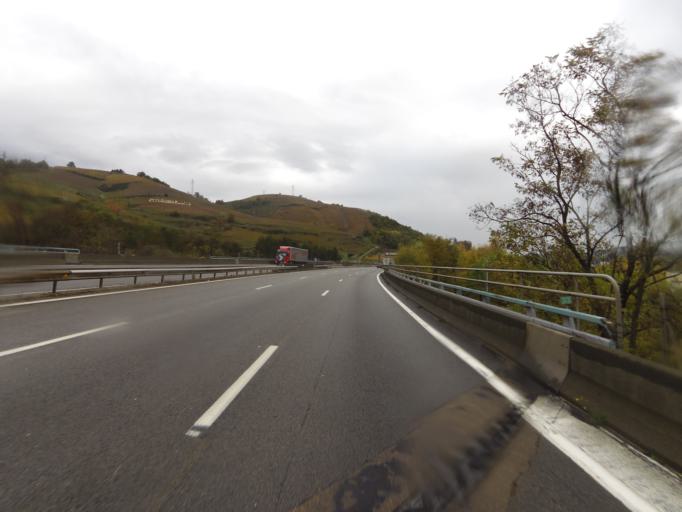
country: FR
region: Rhone-Alpes
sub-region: Departement du Rhone
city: Saint-Cyr-sur-le-Rhone
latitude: 45.5042
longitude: 4.8394
